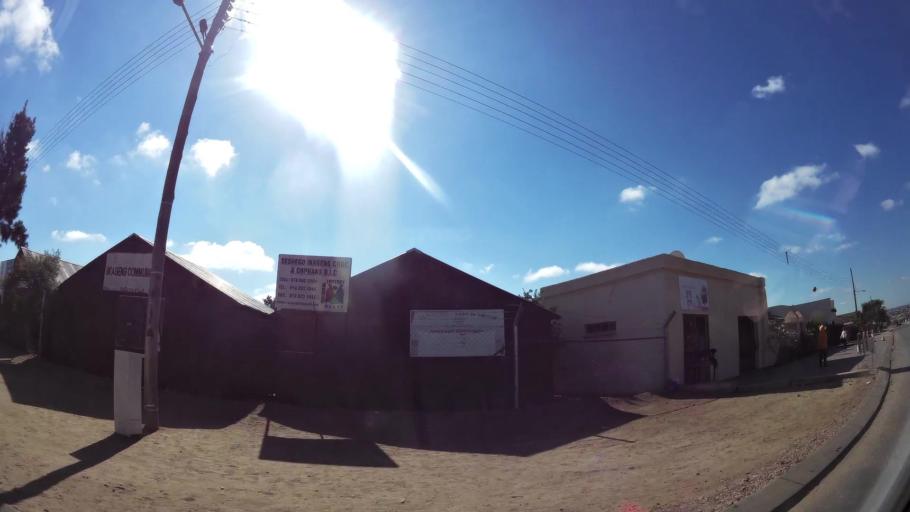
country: ZA
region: Limpopo
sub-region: Capricorn District Municipality
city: Polokwane
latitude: -23.8666
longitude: 29.3864
